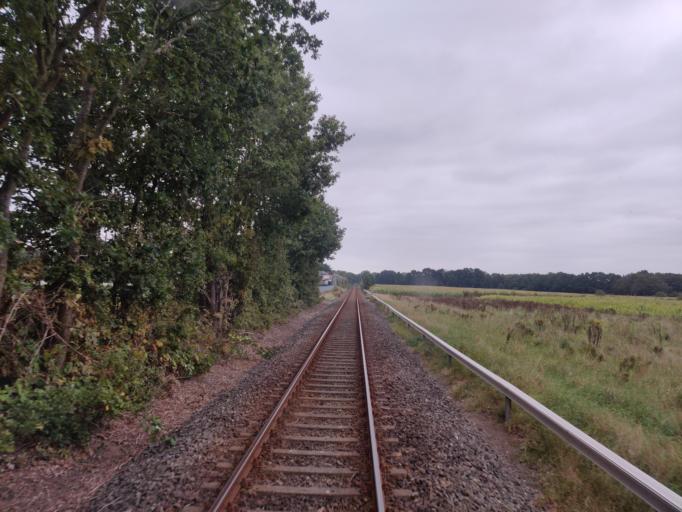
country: DE
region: Lower Saxony
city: Stade
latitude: 53.5699
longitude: 9.4730
